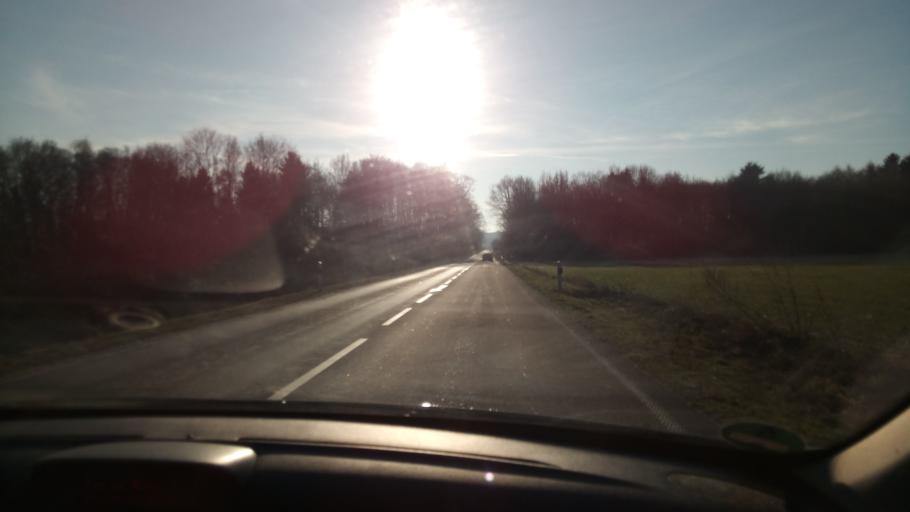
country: DE
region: Schleswig-Holstein
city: Dalldorf
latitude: 53.4390
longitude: 10.6058
